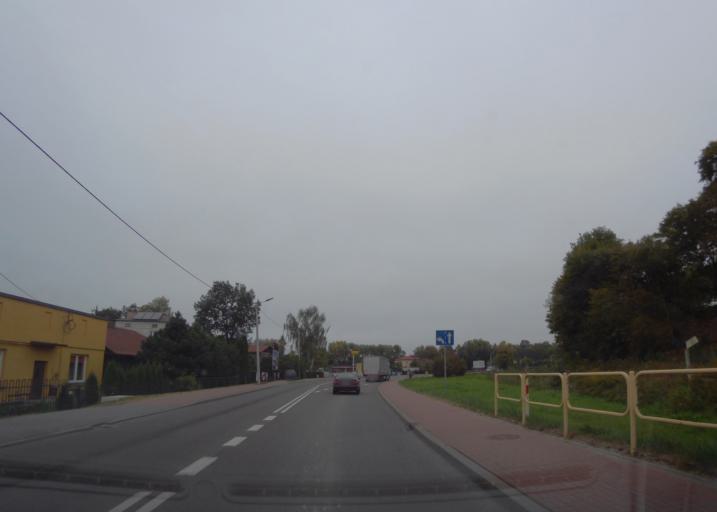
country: PL
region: Lublin Voivodeship
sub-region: Powiat krasnostawski
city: Krasnystaw
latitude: 50.9875
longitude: 23.1821
